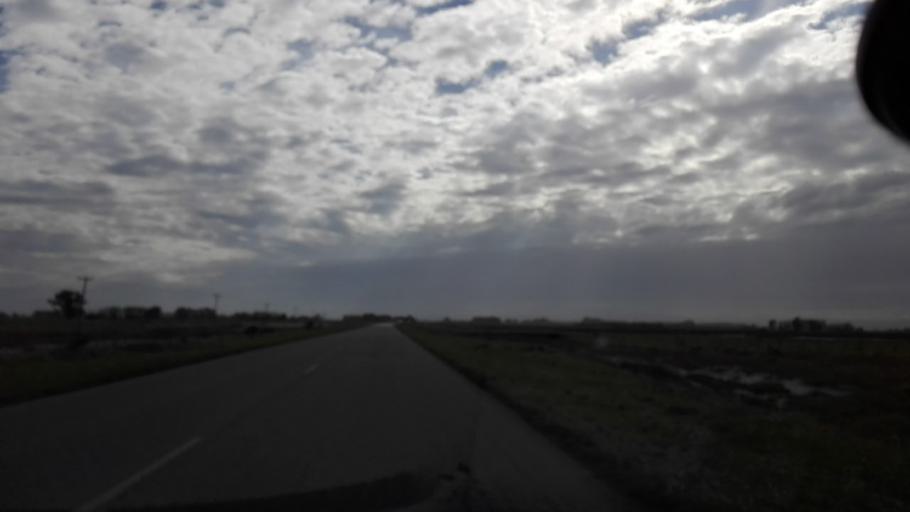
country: AR
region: Buenos Aires
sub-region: Partido de Las Flores
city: Las Flores
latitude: -36.0839
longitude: -59.0901
